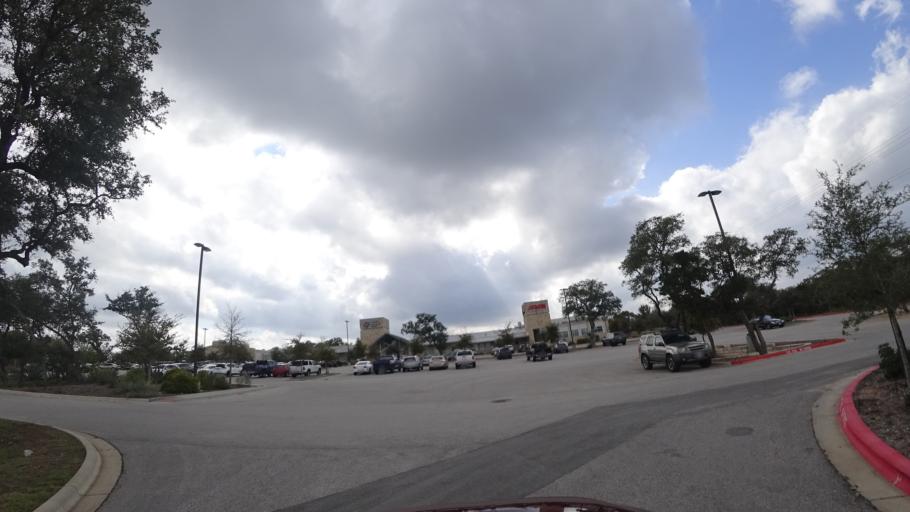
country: US
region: Texas
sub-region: Williamson County
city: Anderson Mill
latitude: 30.4193
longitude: -97.8494
